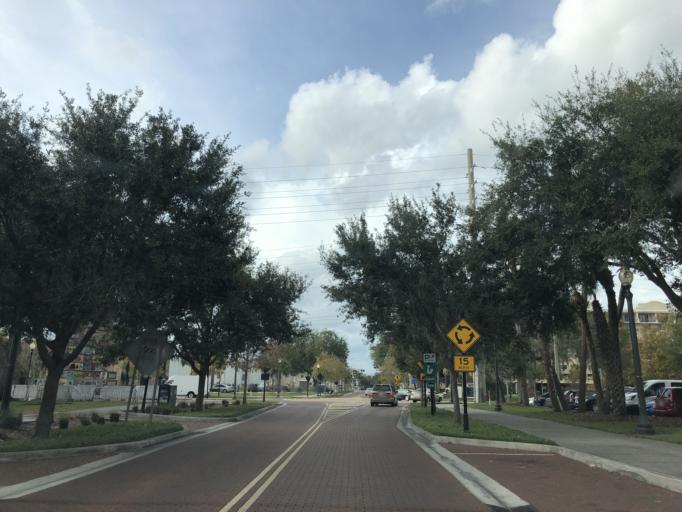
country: US
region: Florida
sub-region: Osceola County
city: Kissimmee
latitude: 28.2915
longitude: -81.4040
